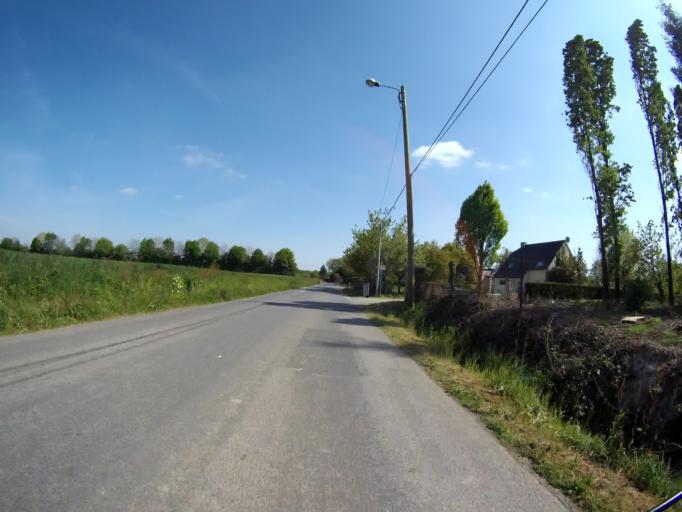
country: FR
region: Brittany
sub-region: Departement d'Ille-et-Vilaine
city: Saint-Erblon
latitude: 48.0212
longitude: -1.6330
